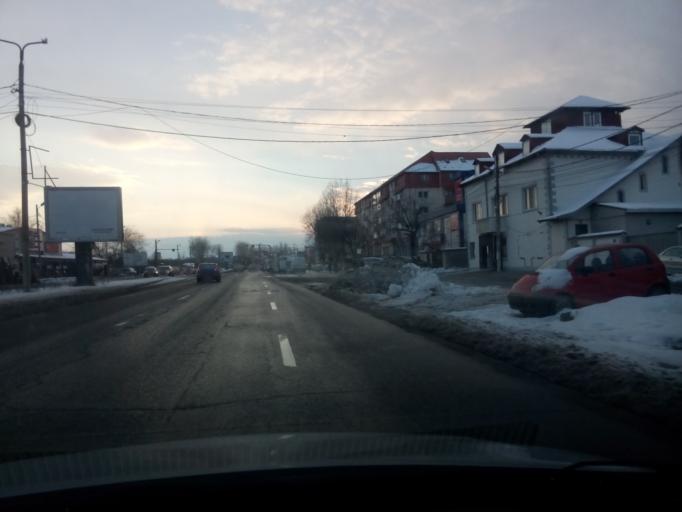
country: RO
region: Ilfov
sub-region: Comuna Pantelimon
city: Pantelimon
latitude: 44.4466
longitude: 26.2027
